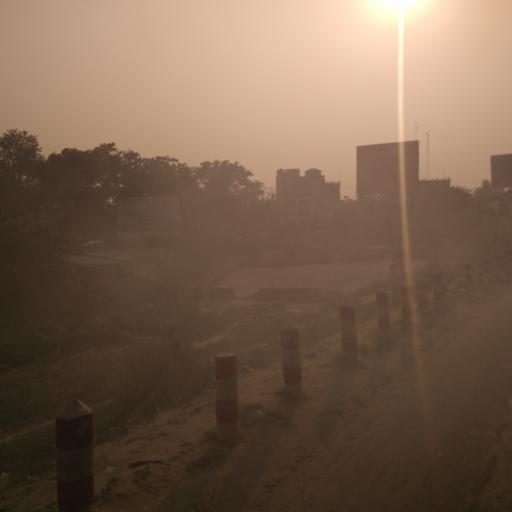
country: BD
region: Dhaka
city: Tungi
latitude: 23.8972
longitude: 90.3329
